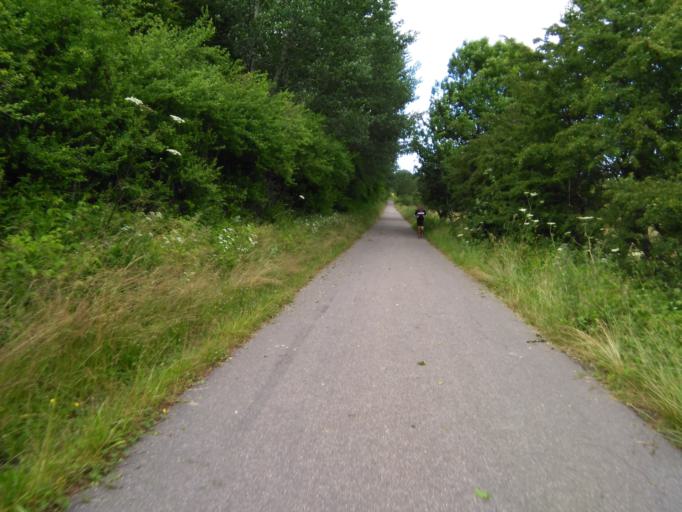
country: DK
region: Central Jutland
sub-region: Arhus Kommune
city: Beder
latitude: 56.0726
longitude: 10.2072
